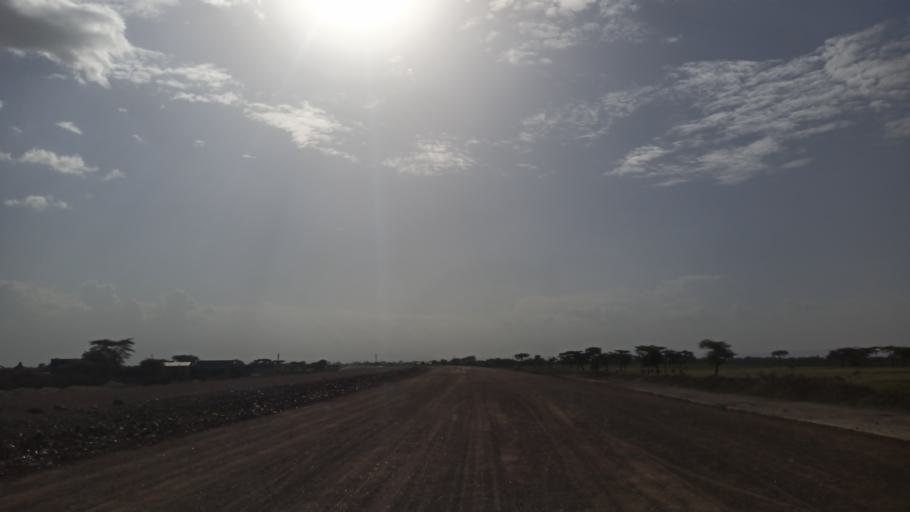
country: ET
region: Oromiya
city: Ziway
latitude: 7.6888
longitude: 38.6647
